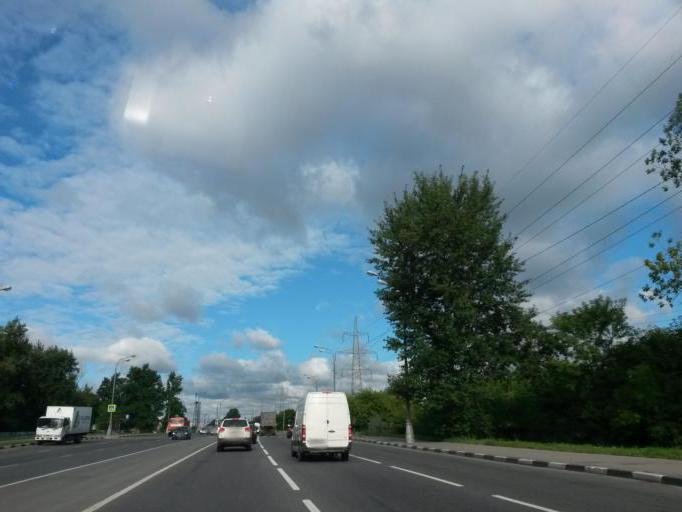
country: RU
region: Moskovskaya
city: Kotel'niki
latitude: 55.6572
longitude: 37.8199
